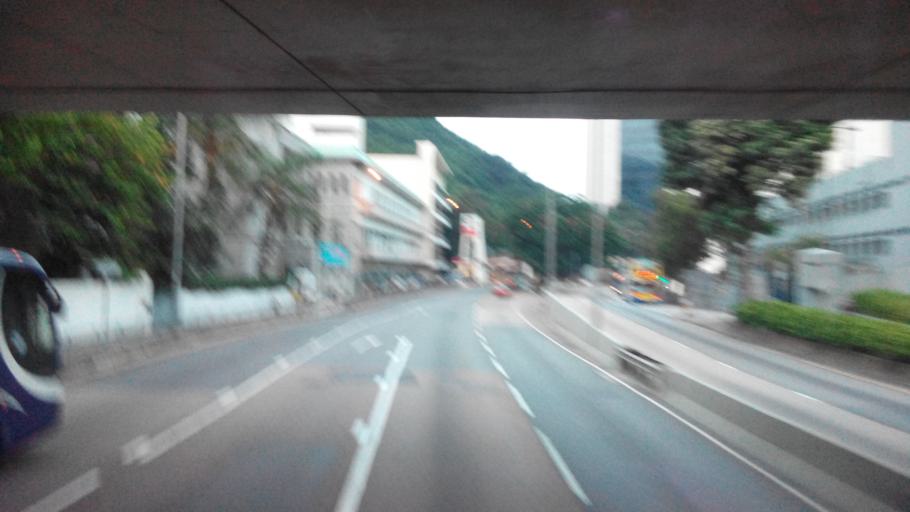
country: HK
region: Central and Western
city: Central
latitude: 22.2483
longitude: 114.1606
